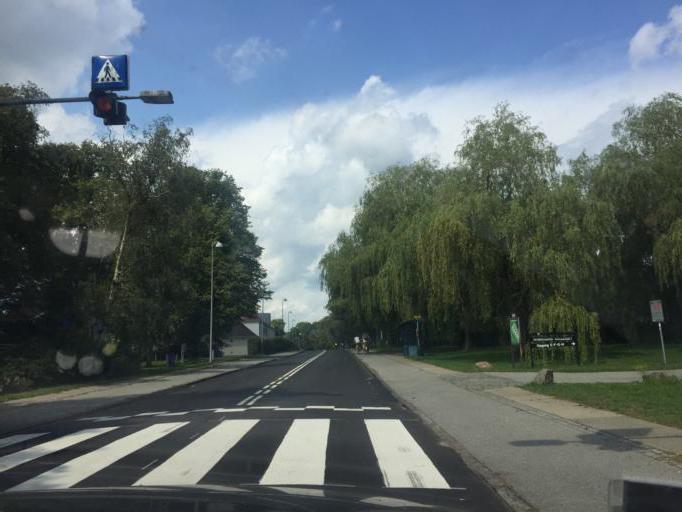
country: DK
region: Capital Region
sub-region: Gladsaxe Municipality
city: Buddinge
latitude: 55.7720
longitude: 12.4743
